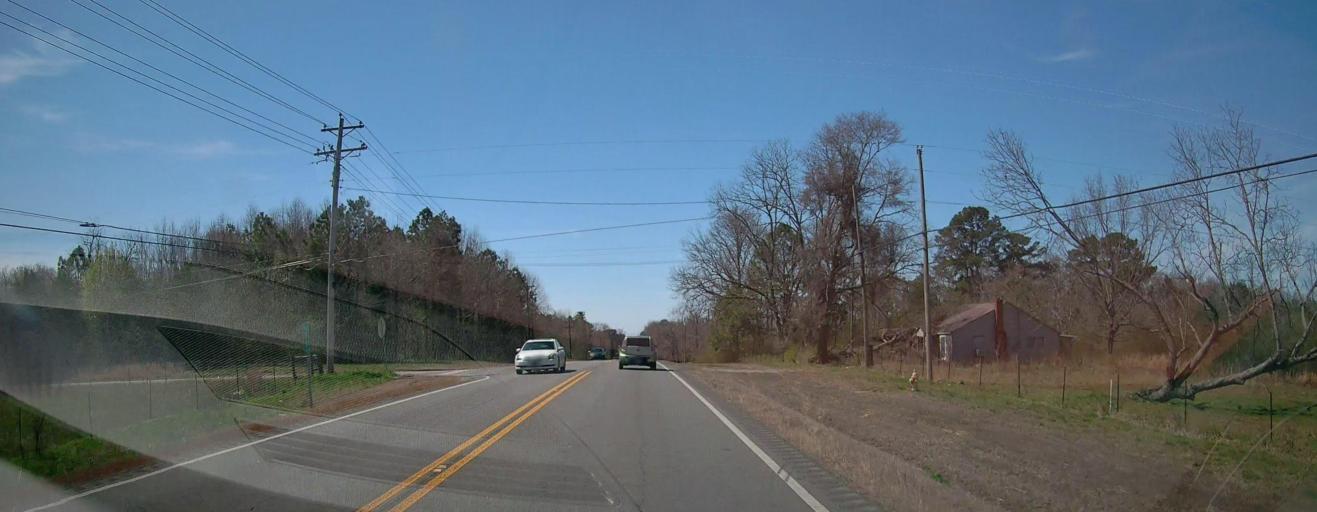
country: US
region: Alabama
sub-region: Blount County
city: Blountsville
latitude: 34.1748
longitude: -86.6438
